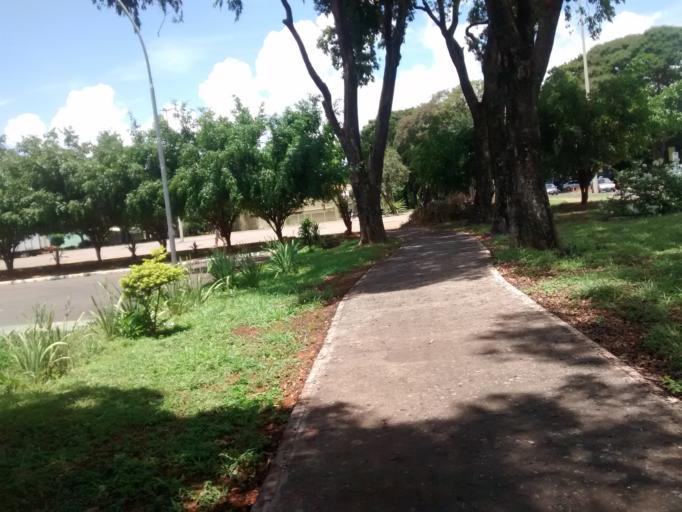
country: BR
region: Federal District
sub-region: Brasilia
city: Brasilia
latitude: -15.8019
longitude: -47.8983
